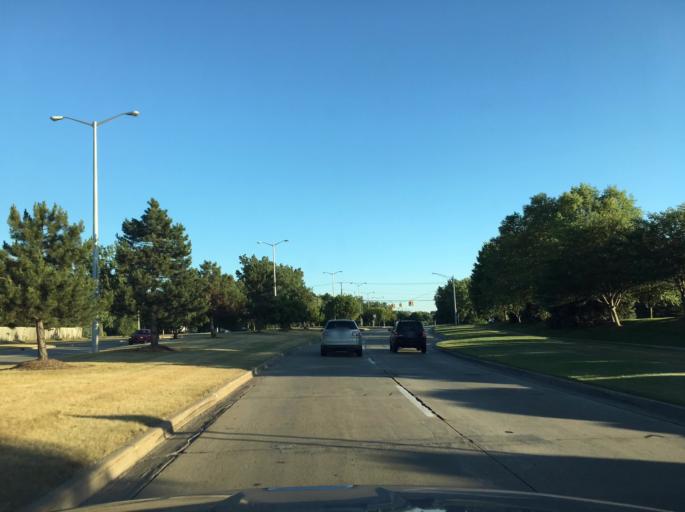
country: US
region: Michigan
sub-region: Macomb County
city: Sterling Heights
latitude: 42.5899
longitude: -82.9915
